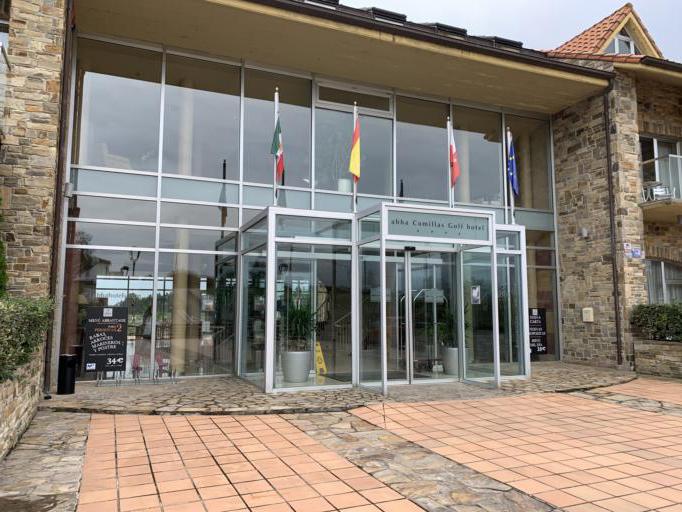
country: ES
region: Cantabria
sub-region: Provincia de Cantabria
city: Comillas
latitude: 43.3825
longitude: -4.2825
